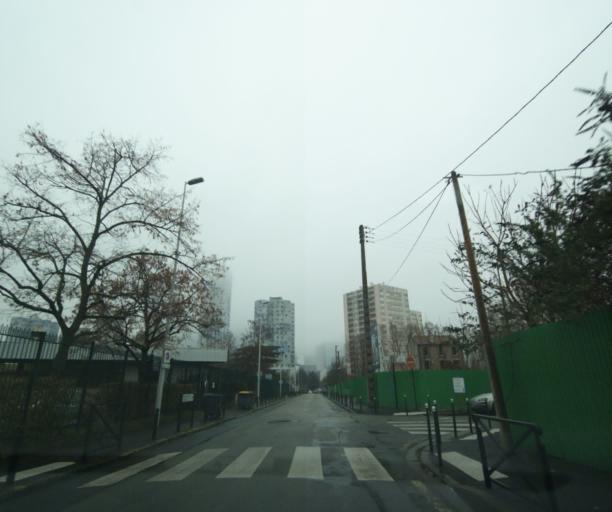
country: FR
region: Ile-de-France
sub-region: Departement des Hauts-de-Seine
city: Puteaux
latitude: 48.8863
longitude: 2.2258
